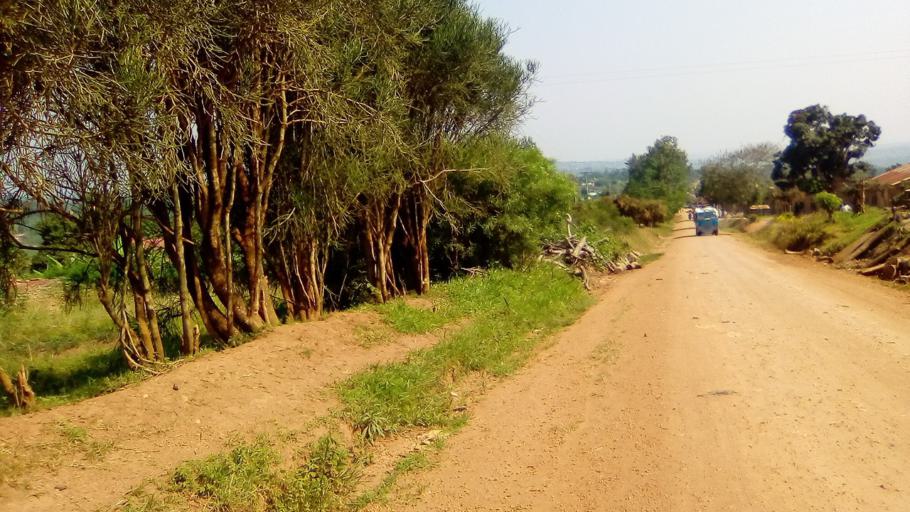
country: UG
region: Central Region
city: Masaka
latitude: -0.2715
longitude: 31.6453
